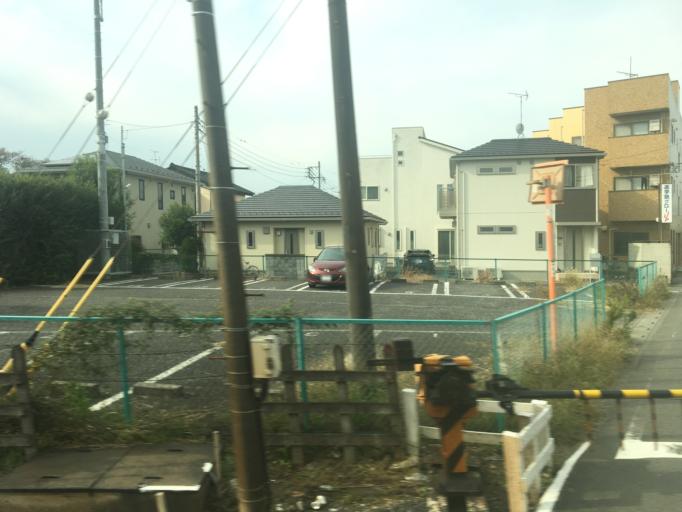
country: JP
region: Saitama
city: Sayama
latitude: 35.8344
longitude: 139.4251
